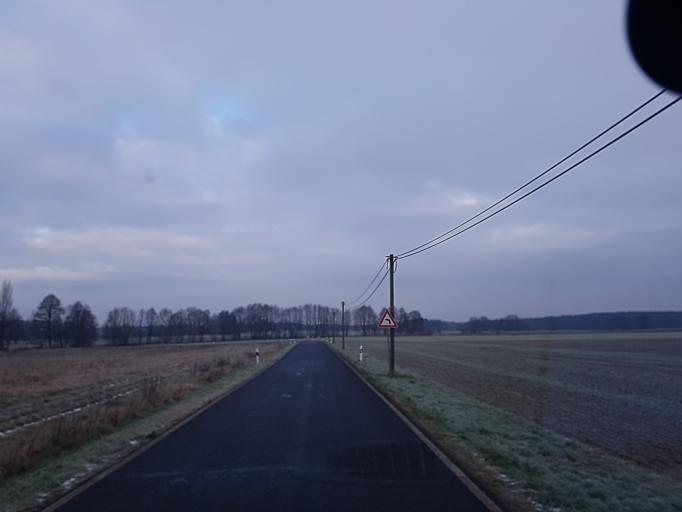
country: DE
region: Brandenburg
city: Crinitz
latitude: 51.7285
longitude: 13.8374
